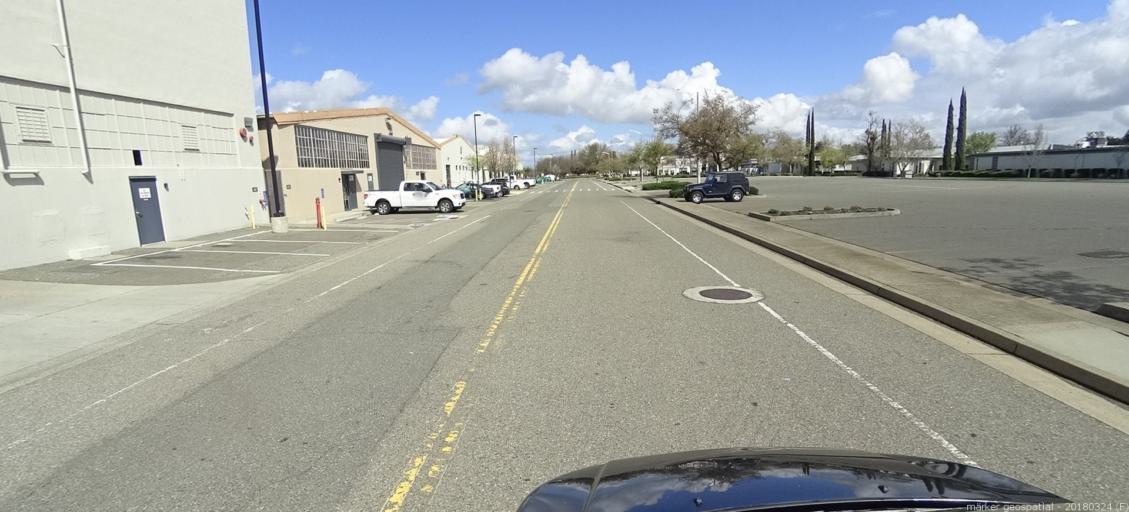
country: US
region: California
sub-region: Sacramento County
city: North Highlands
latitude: 38.6584
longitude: -121.3862
